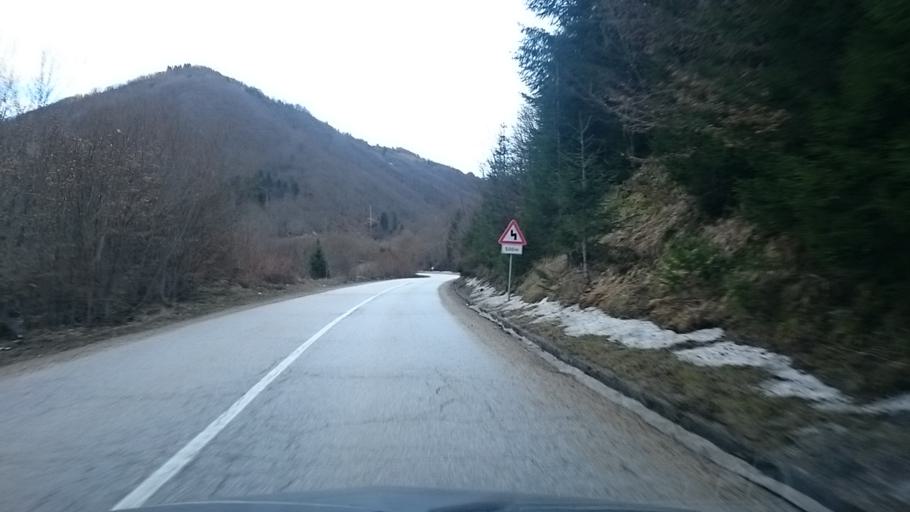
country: BA
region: Republika Srpska
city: Skender Vakuf
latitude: 44.4269
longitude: 17.4081
